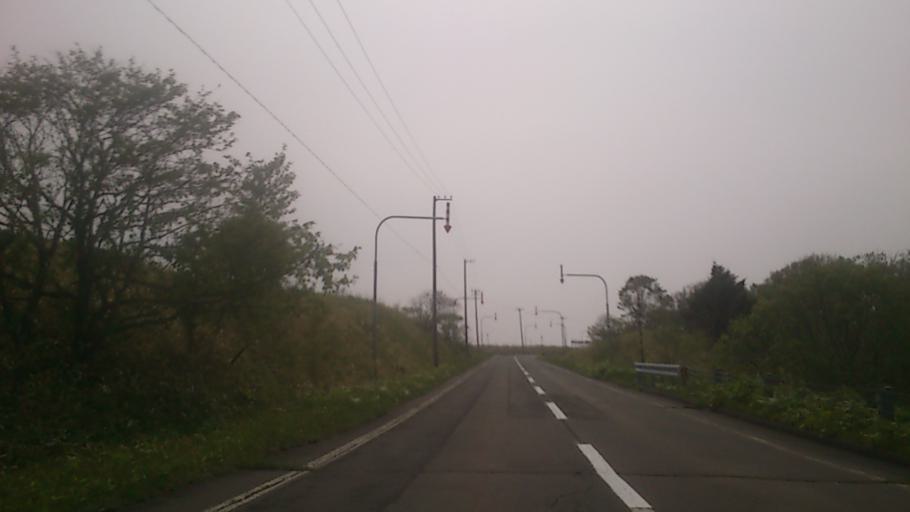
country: JP
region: Hokkaido
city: Nemuro
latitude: 43.1755
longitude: 145.3192
